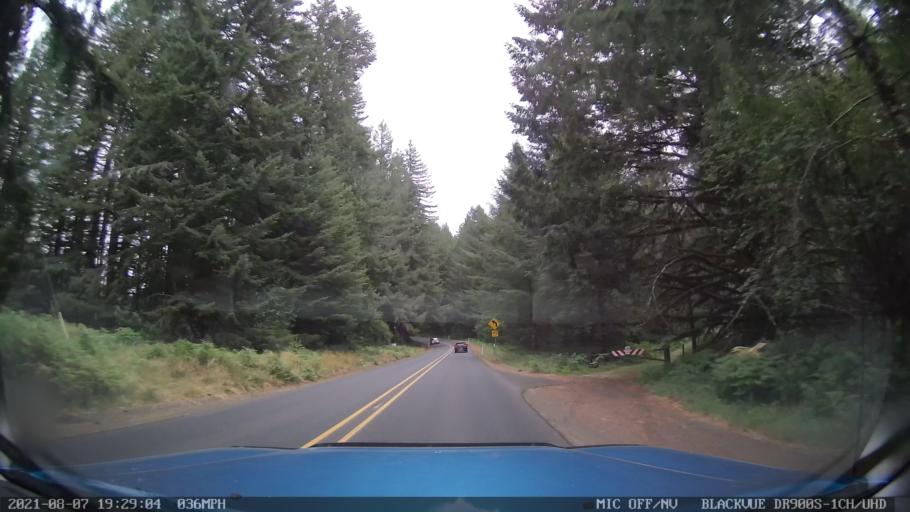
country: US
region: Oregon
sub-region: Linn County
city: Lyons
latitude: 44.8838
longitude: -122.6337
